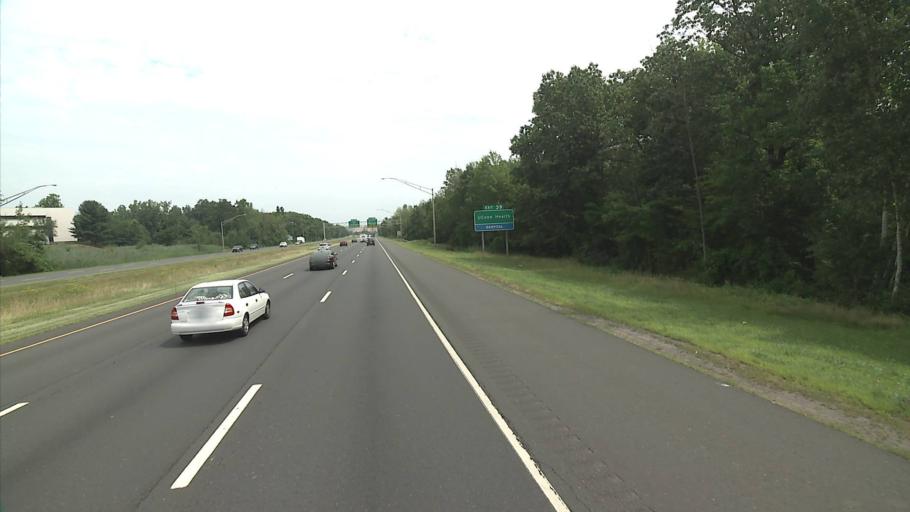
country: US
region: Connecticut
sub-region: Hartford County
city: Farmington
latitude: 41.7097
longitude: -72.8005
